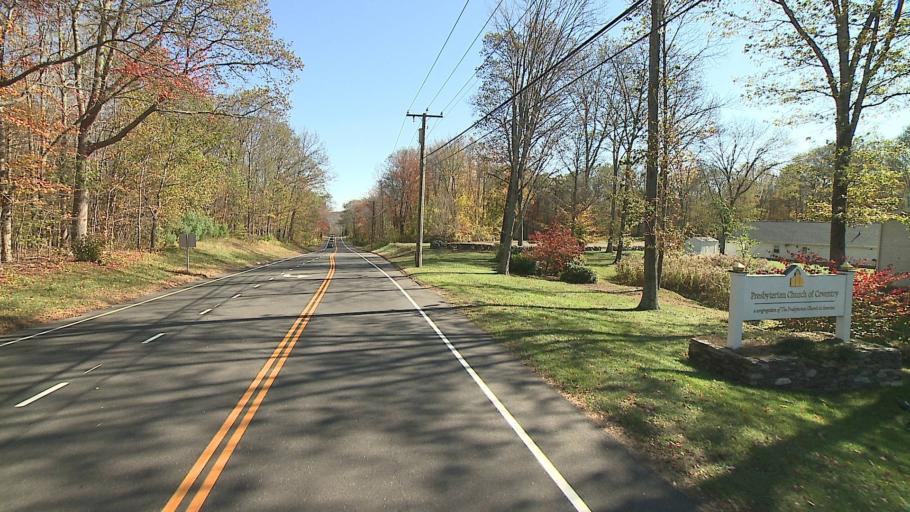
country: US
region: Connecticut
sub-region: Tolland County
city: Coventry Lake
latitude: 41.7987
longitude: -72.3612
